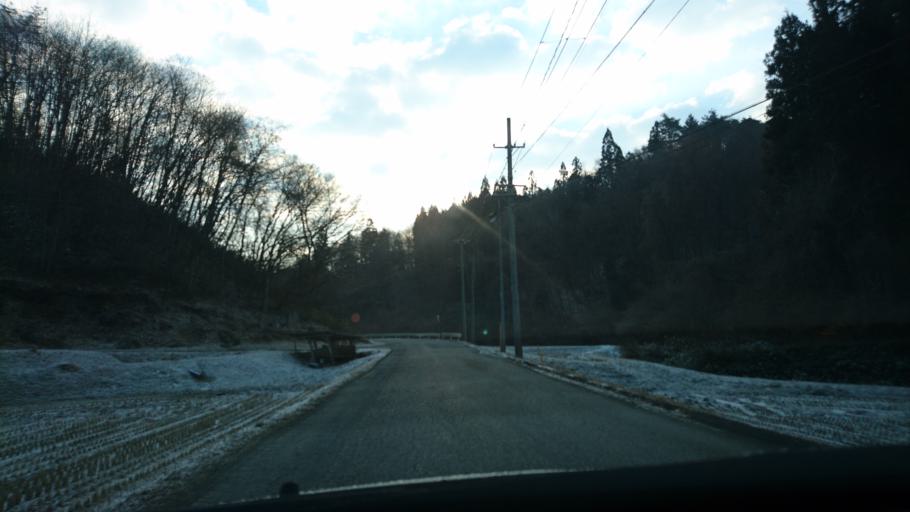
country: JP
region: Iwate
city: Ichinoseki
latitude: 38.9191
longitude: 141.3548
